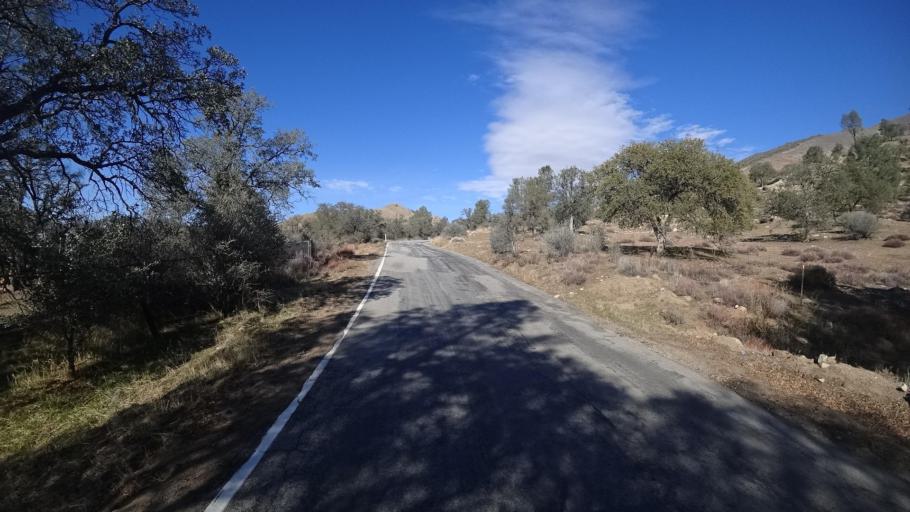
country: US
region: California
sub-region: Kern County
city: Bodfish
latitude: 35.5448
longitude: -118.5073
